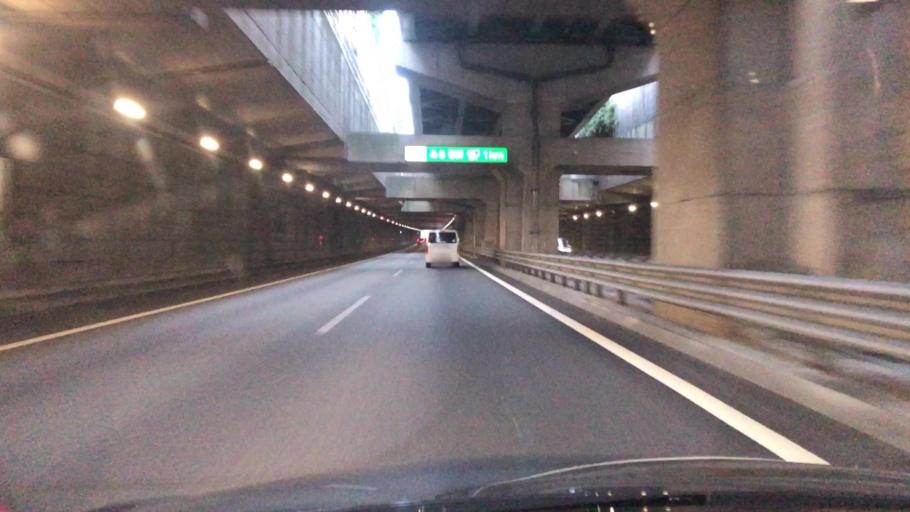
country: JP
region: Tokyo
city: Fussa
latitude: 35.7280
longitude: 139.2836
